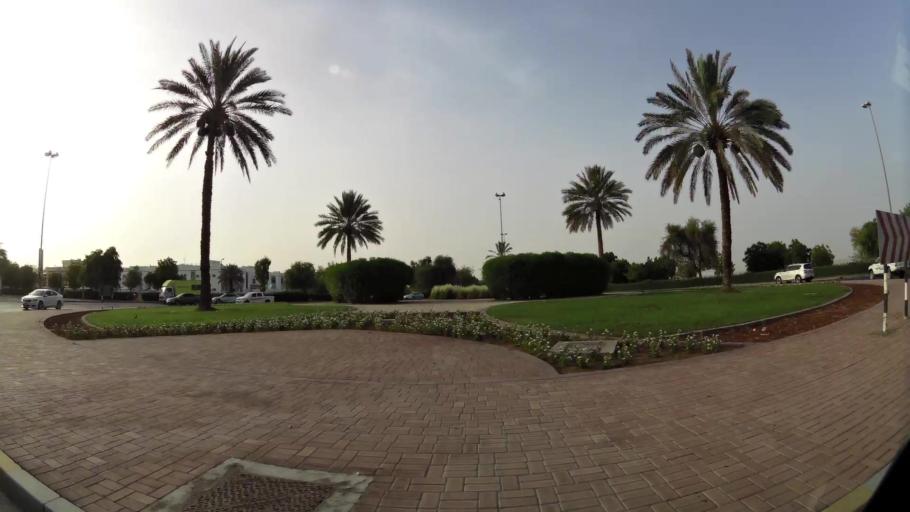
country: OM
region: Al Buraimi
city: Al Buraymi
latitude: 24.2406
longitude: 55.7520
